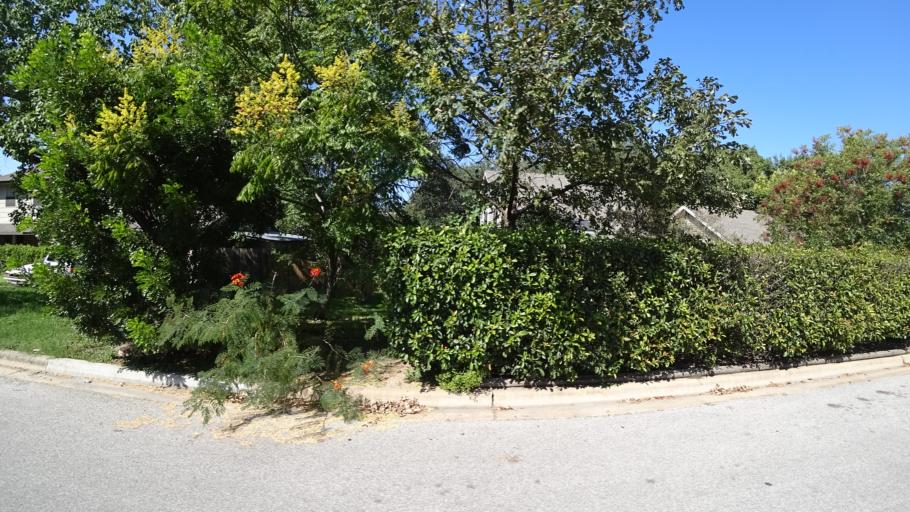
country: US
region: Texas
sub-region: Travis County
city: Rollingwood
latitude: 30.2544
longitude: -97.7901
